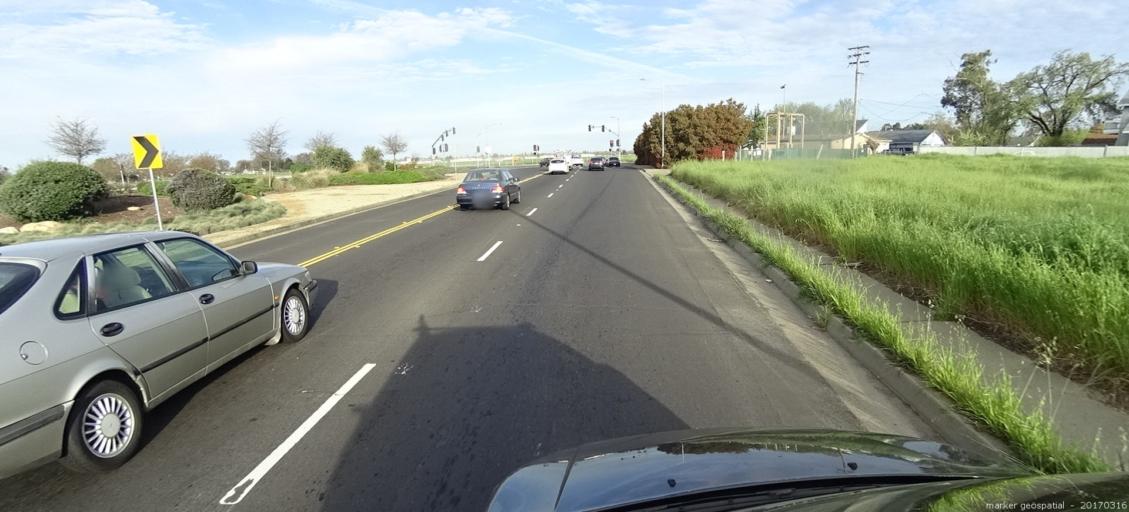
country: US
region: California
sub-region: Sacramento County
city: Parkway
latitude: 38.5104
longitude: -121.4819
